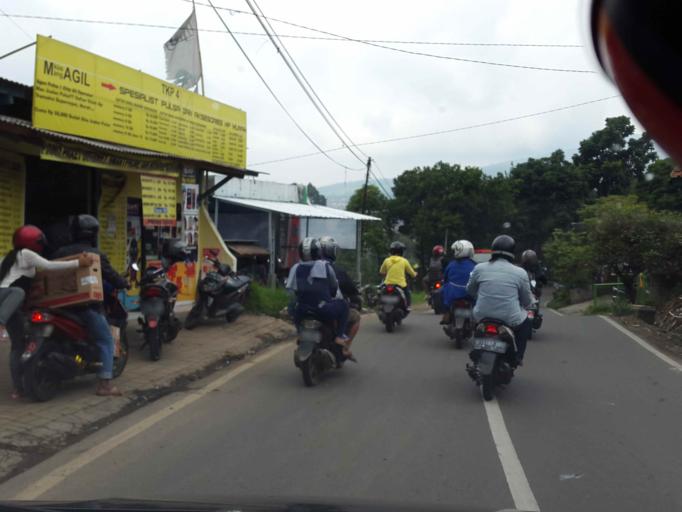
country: ID
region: West Java
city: Lembang
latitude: -6.8191
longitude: 107.6033
